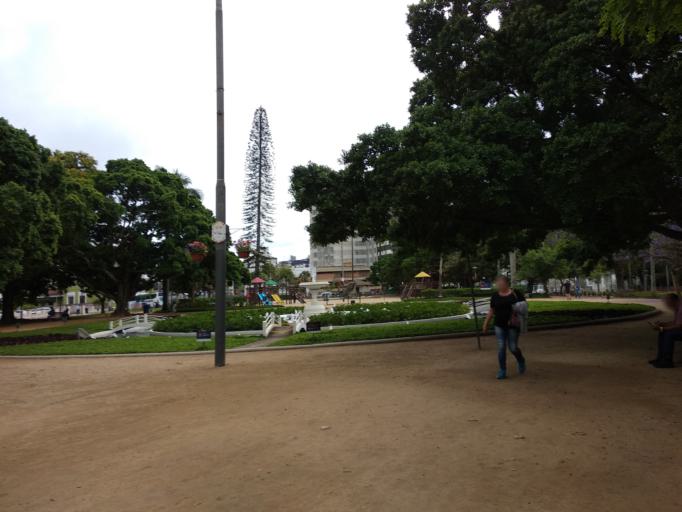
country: BR
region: Santa Catarina
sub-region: Florianopolis
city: Florianopolis
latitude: -27.5933
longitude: -48.5467
